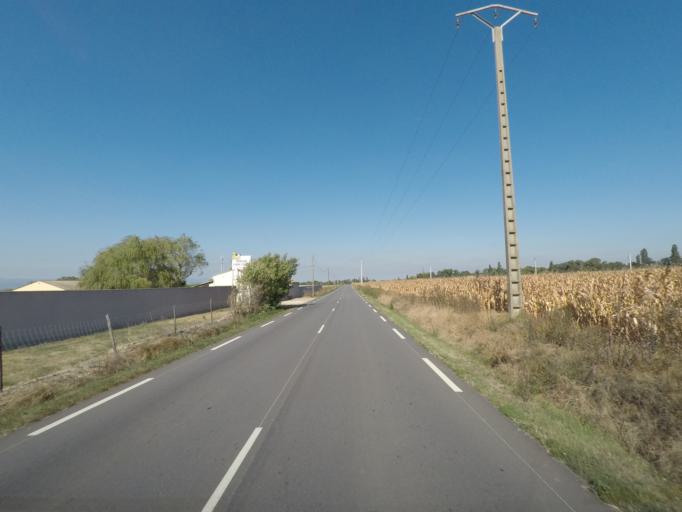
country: FR
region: Rhone-Alpes
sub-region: Departement de la Drome
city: Upie
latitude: 44.8026
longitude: 5.0154
